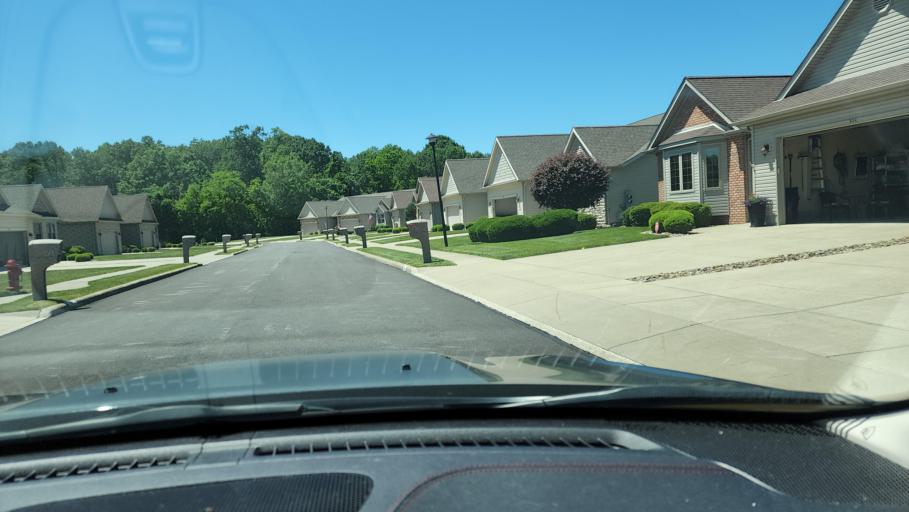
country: US
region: Ohio
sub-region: Trumbull County
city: McKinley Heights
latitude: 41.1935
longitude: -80.7387
